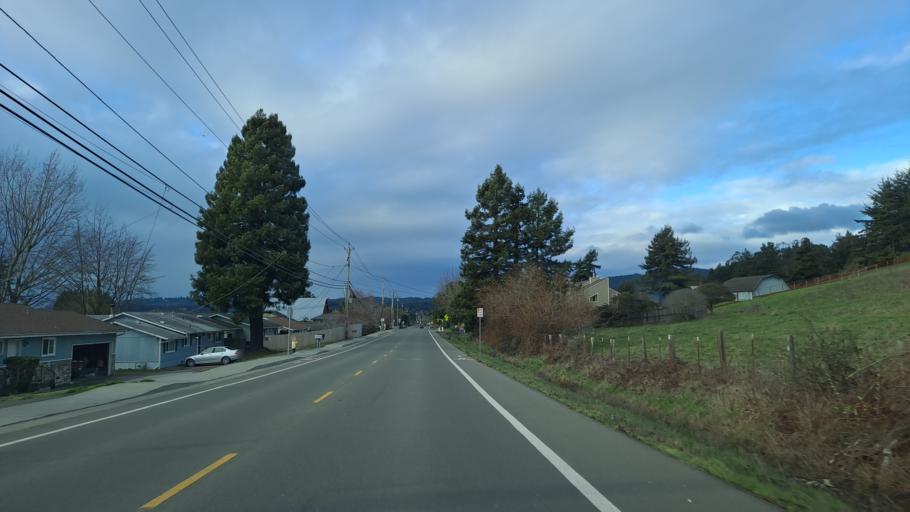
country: US
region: California
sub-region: Humboldt County
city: Fortuna
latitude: 40.5749
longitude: -124.1284
